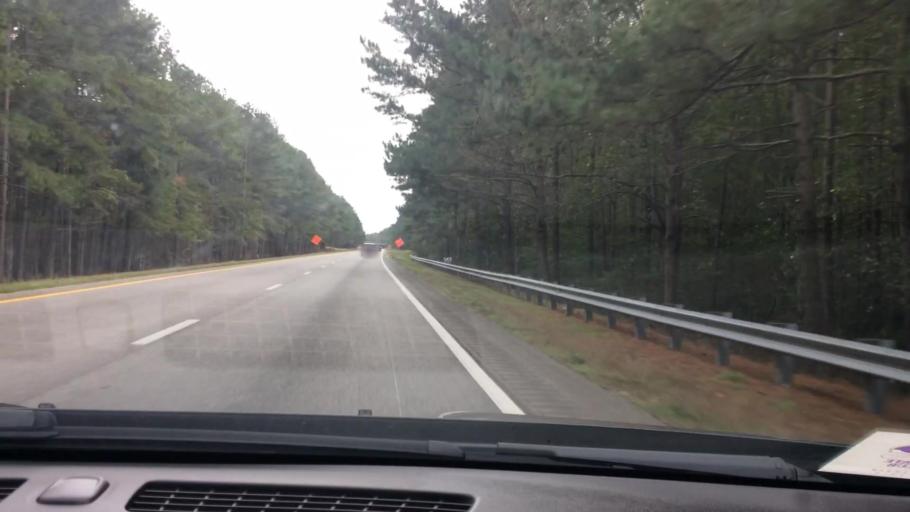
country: US
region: North Carolina
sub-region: Nash County
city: Spring Hope
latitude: 35.7919
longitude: -78.1488
